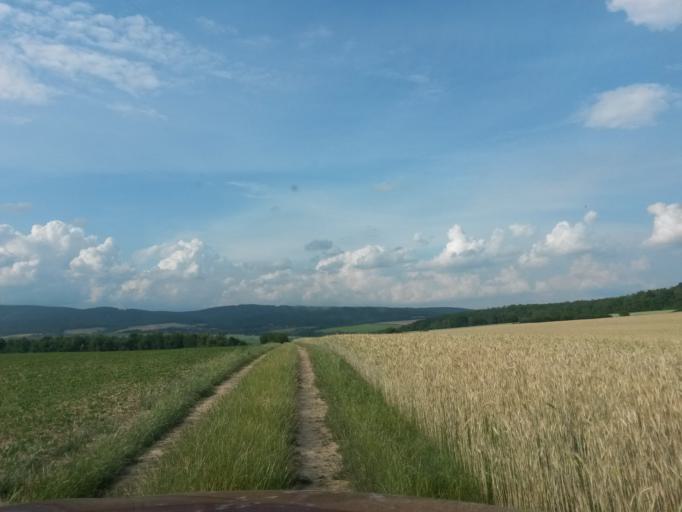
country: SK
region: Kosicky
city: Moldava nad Bodvou
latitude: 48.6427
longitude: 21.1087
